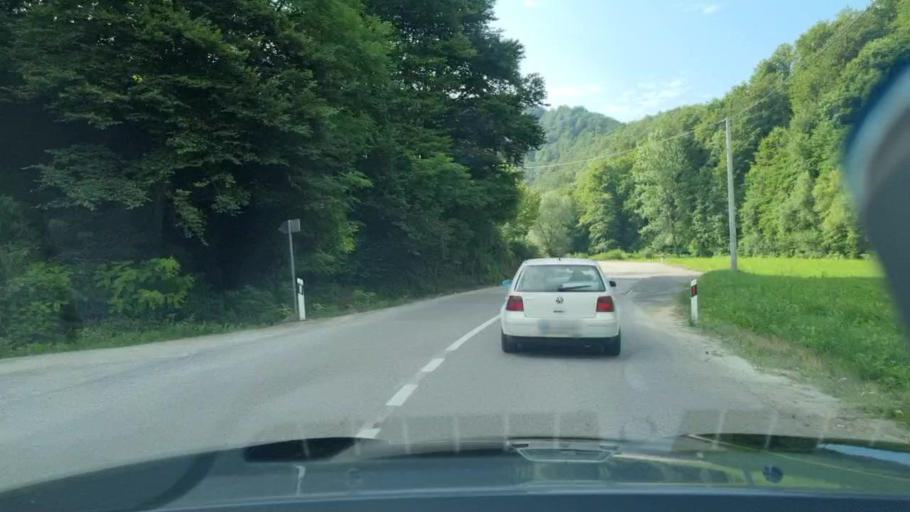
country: BA
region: Federation of Bosnia and Herzegovina
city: Jezerski
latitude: 45.0086
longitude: 16.1208
